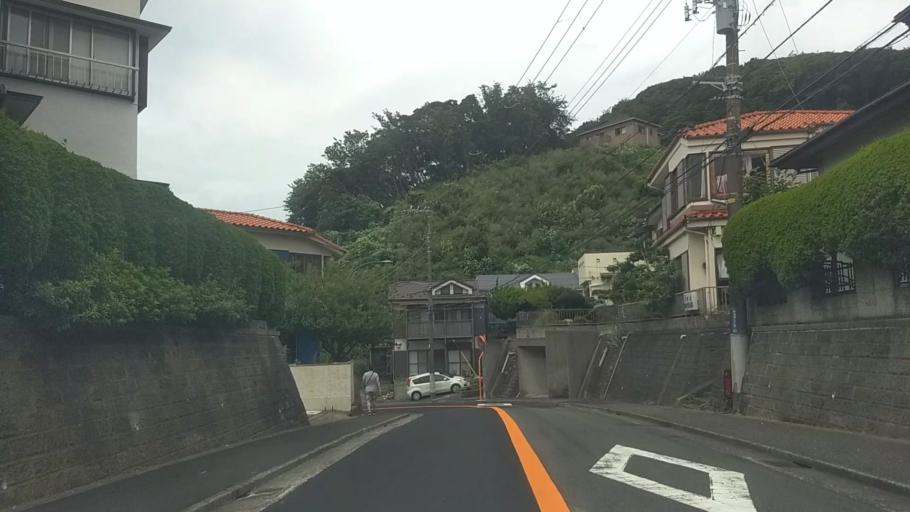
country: JP
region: Kanagawa
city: Yokosuka
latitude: 35.2444
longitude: 139.7255
